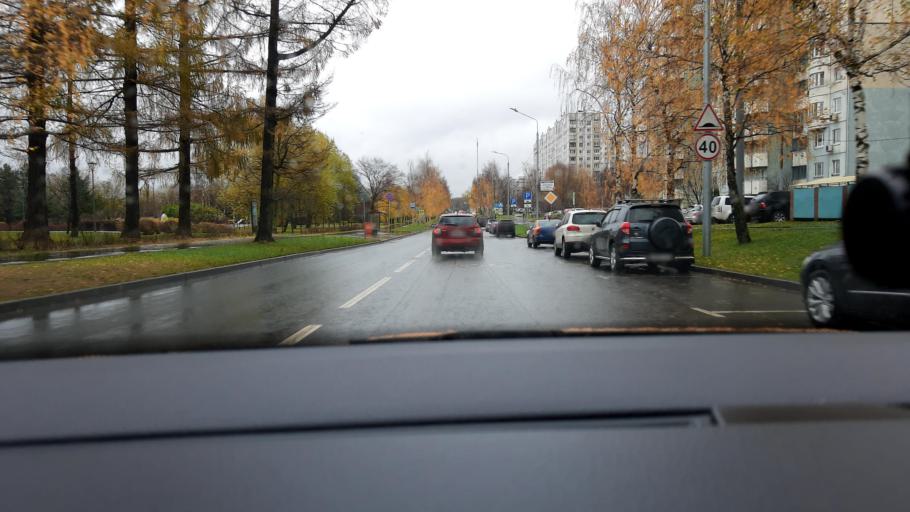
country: RU
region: Moscow
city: Lianozovo
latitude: 55.9070
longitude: 37.5802
